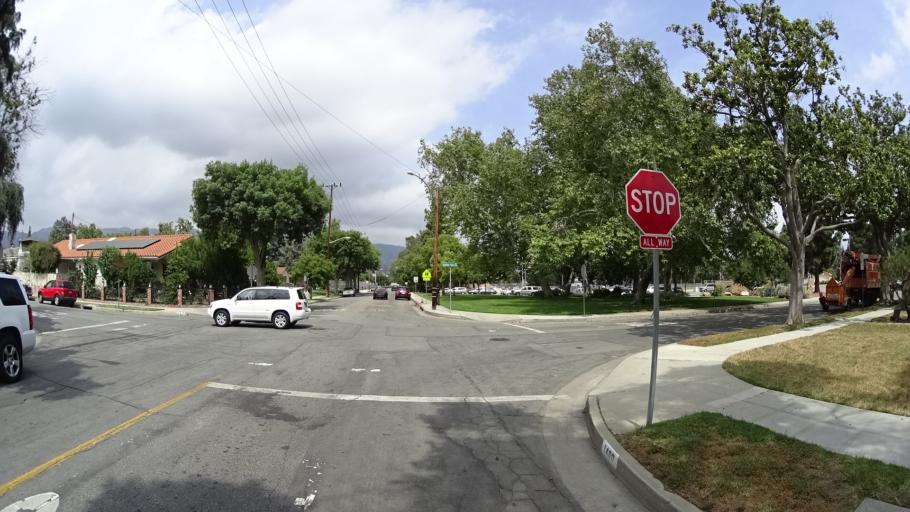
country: US
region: California
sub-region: Los Angeles County
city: Burbank
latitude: 34.1722
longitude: -118.3220
